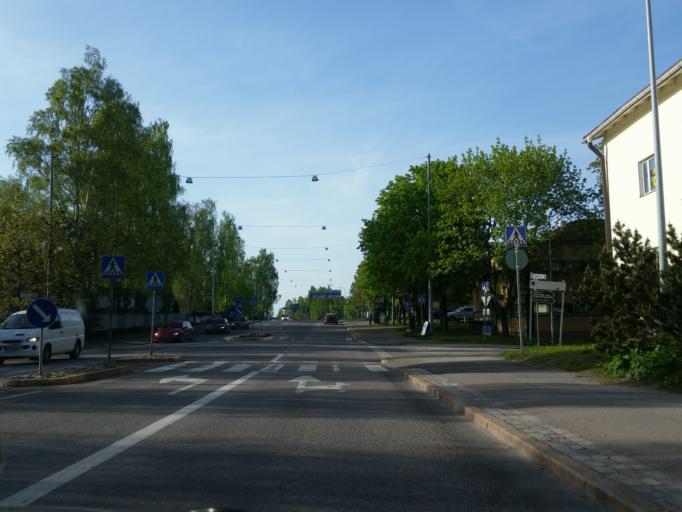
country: FI
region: Uusimaa
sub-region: Helsinki
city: Helsinki
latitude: 60.2385
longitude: 24.9284
